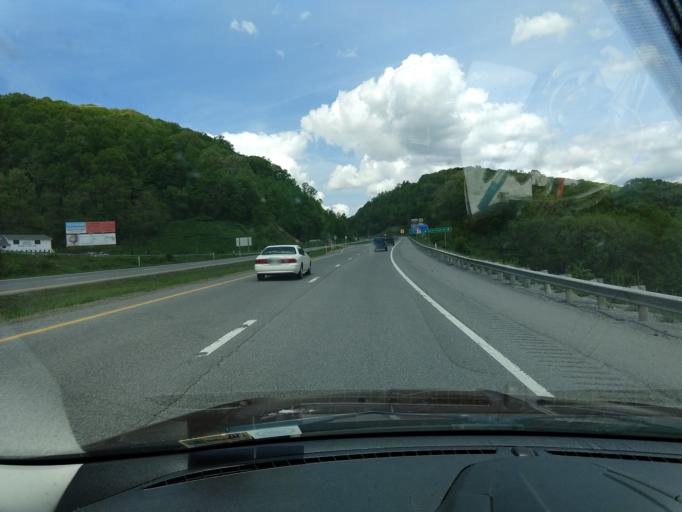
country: US
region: West Virginia
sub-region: Mercer County
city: Bluefield
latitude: 37.2868
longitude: -81.1666
